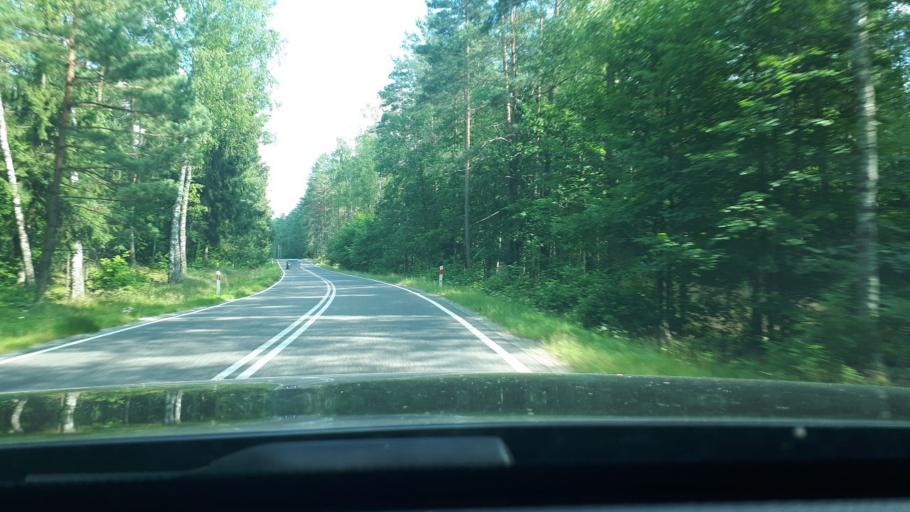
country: PL
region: Warmian-Masurian Voivodeship
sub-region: Powiat olsztynski
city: Stawiguda
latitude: 53.5365
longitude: 20.4282
